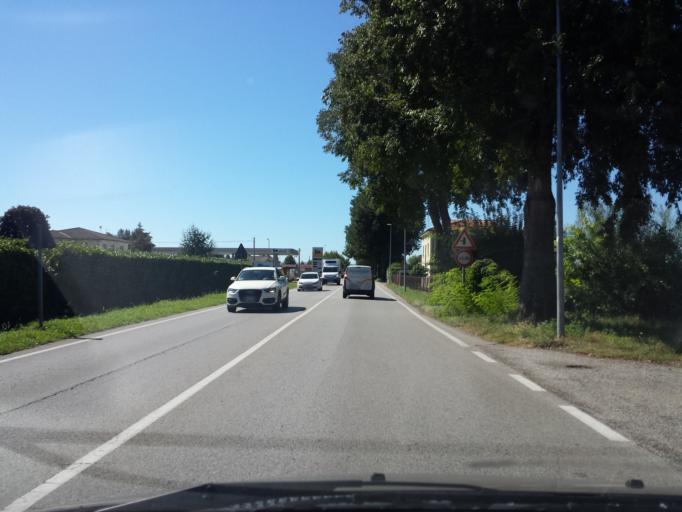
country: IT
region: Veneto
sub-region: Provincia di Vicenza
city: Dueville
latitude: 45.6211
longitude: 11.5685
